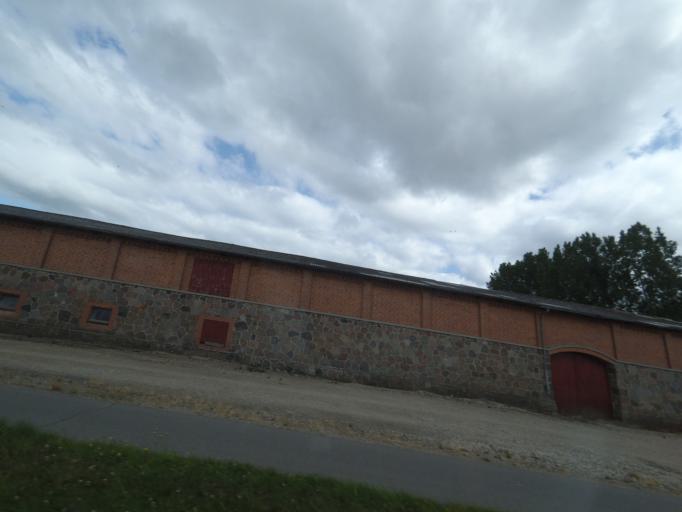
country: DK
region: South Denmark
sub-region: Nordfyns Kommune
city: Otterup
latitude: 55.5247
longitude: 10.4175
